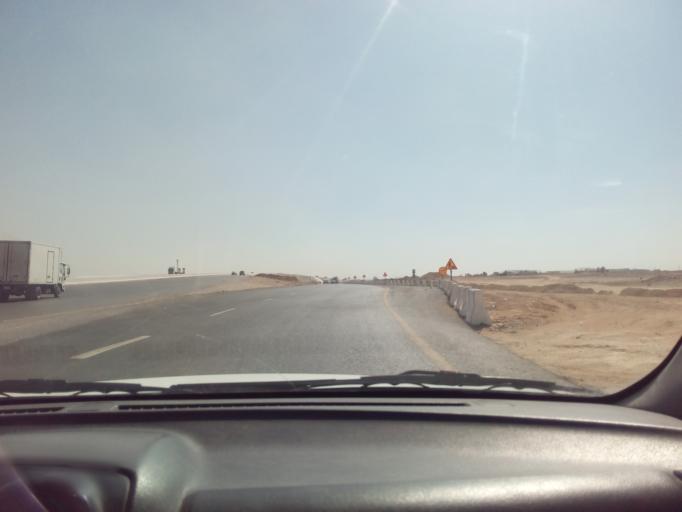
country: SA
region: Ar Riyad
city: Riyadh
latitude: 24.5985
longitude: 46.8869
